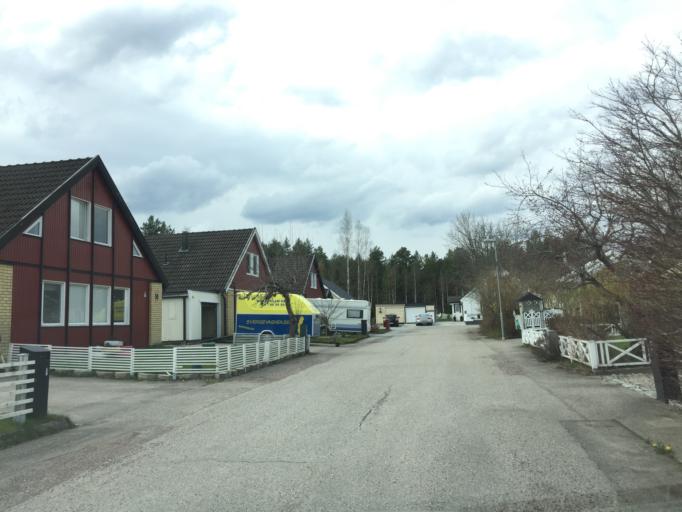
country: SE
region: OErebro
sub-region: Orebro Kommun
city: Orebro
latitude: 59.3111
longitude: 15.1783
